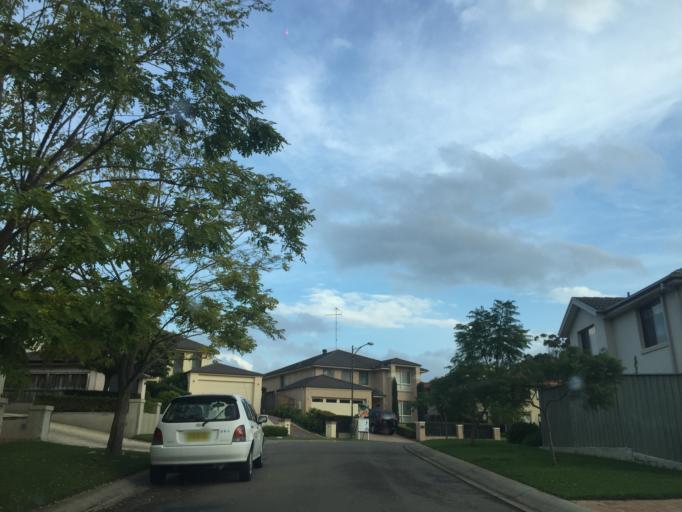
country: AU
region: New South Wales
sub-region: The Hills Shire
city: Glenhaven
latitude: -33.7016
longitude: 150.9765
